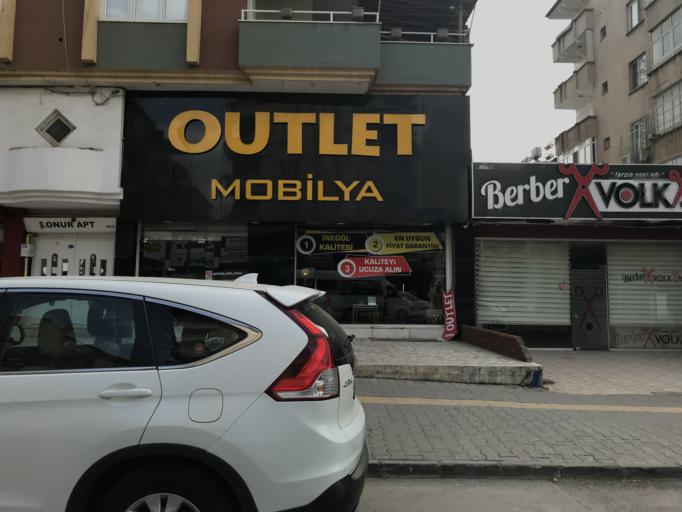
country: TR
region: Gaziantep
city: Sahinbey
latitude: 37.0529
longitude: 37.3350
